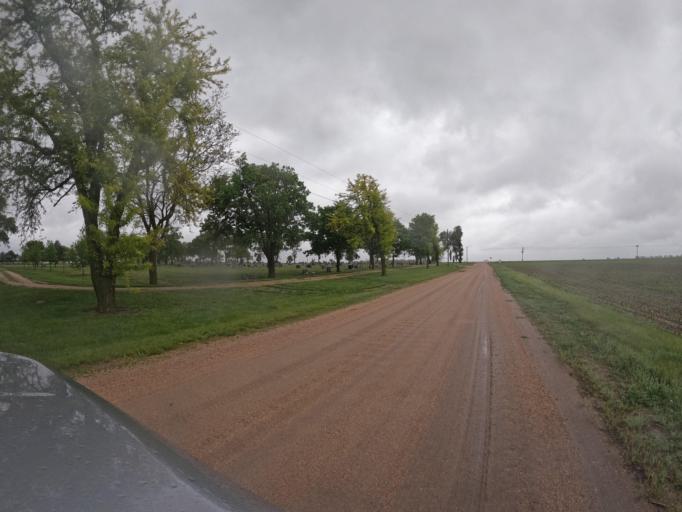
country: US
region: Nebraska
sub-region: Clay County
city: Harvard
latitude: 40.6131
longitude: -98.0945
